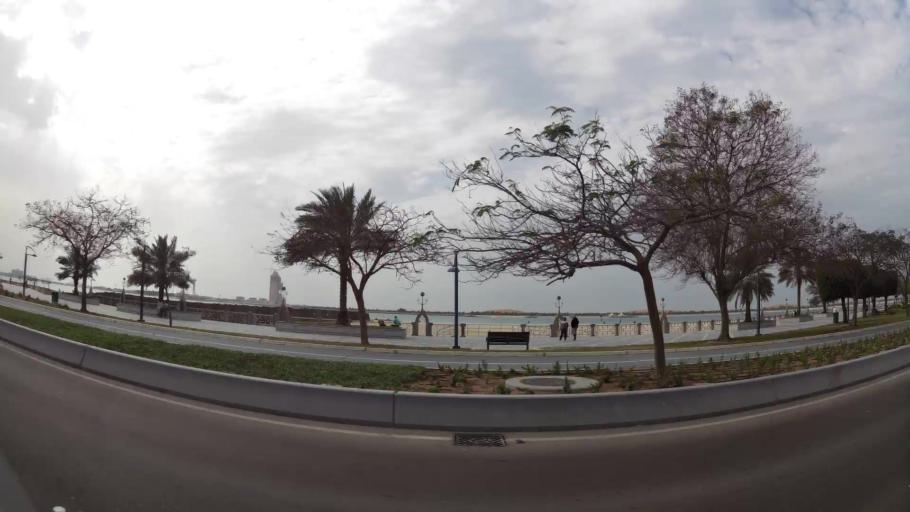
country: AE
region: Abu Dhabi
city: Abu Dhabi
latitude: 24.4807
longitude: 54.3466
